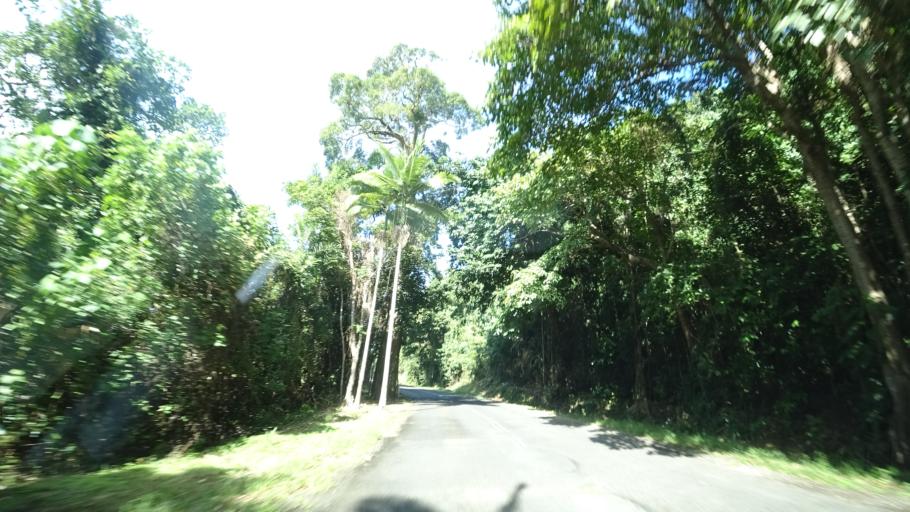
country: AU
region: Queensland
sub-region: Cairns
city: Port Douglas
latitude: -16.1593
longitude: 145.4429
